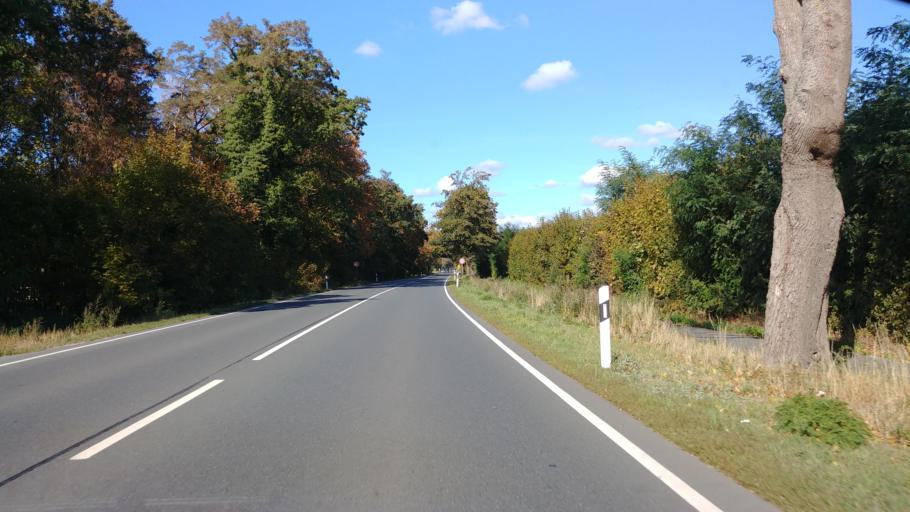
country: DE
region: Lower Saxony
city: Didderse
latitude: 52.3620
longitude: 10.3937
